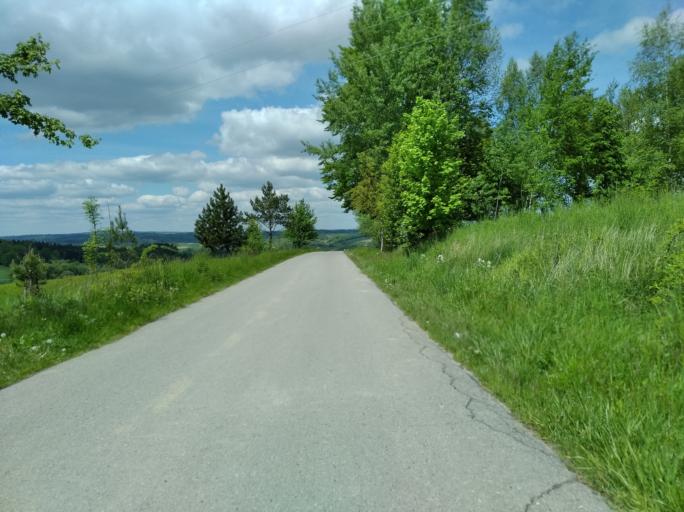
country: PL
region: Subcarpathian Voivodeship
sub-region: Powiat ropczycko-sedziszowski
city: Wielopole Skrzynskie
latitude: 49.9254
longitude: 21.6044
